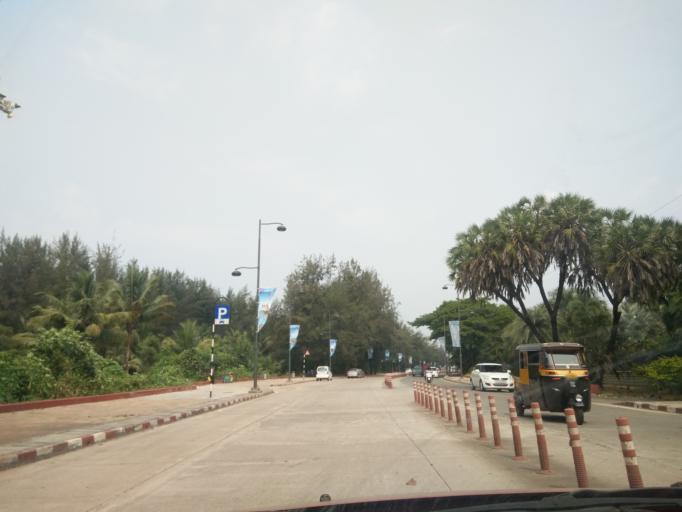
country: IN
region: Goa
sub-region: North Goa
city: Taleigao
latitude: 15.4755
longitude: 73.8083
